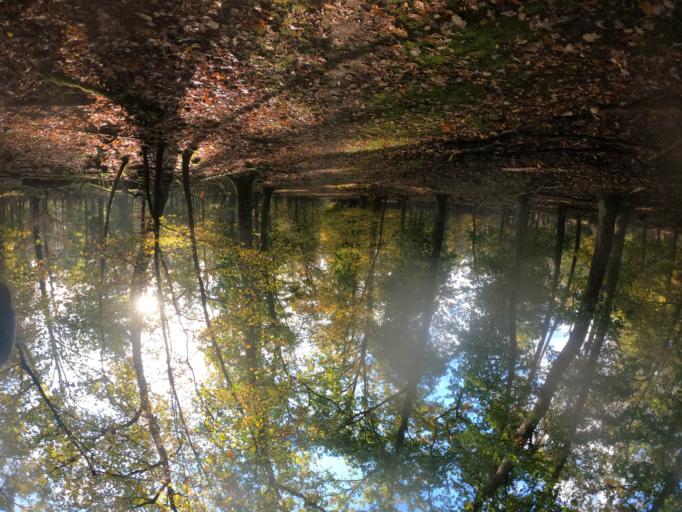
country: DE
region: Hesse
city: Raunheim
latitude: 50.0000
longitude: 8.4969
